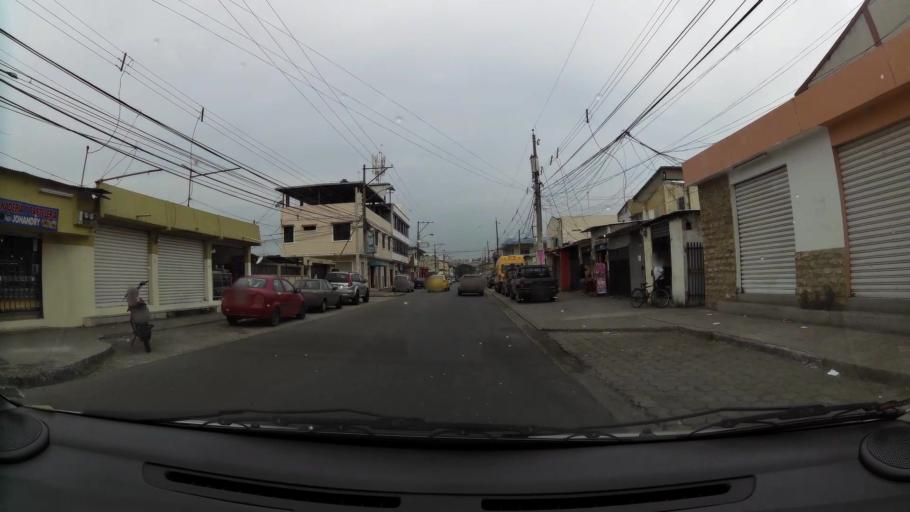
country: EC
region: Guayas
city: Eloy Alfaro
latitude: -2.1410
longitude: -79.9006
